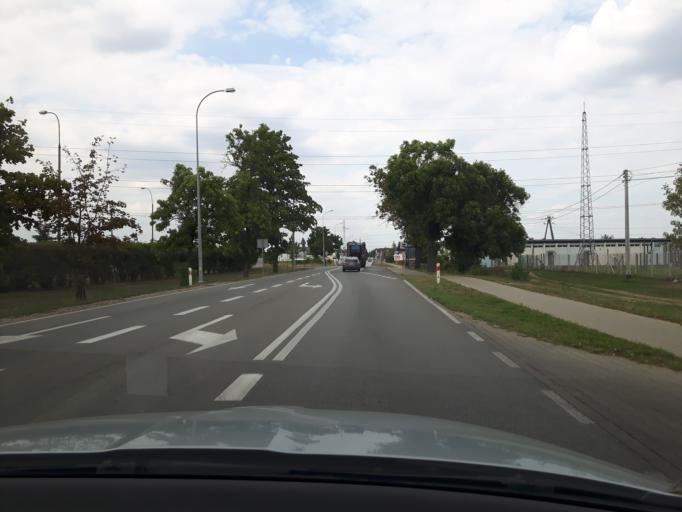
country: PL
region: Masovian Voivodeship
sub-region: Powiat legionowski
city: Stanislawow Pierwszy
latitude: 52.3702
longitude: 21.0289
